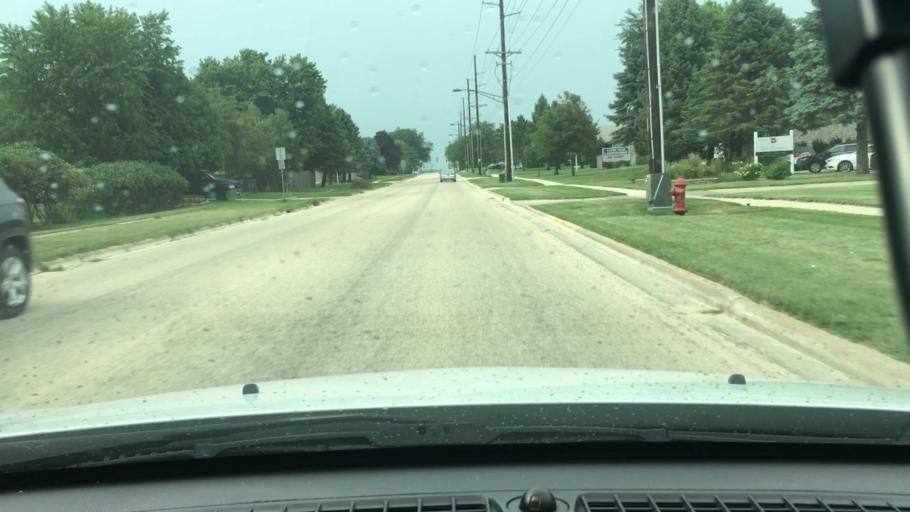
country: US
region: Illinois
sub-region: Ogle County
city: Rochelle
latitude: 41.9300
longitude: -89.0545
